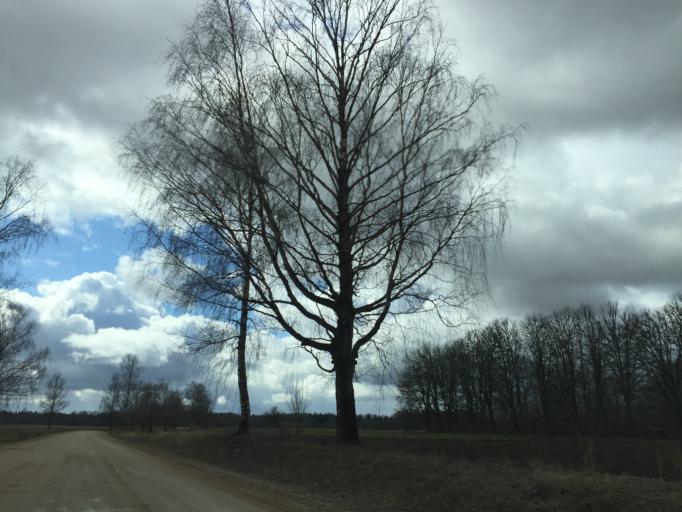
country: LV
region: Akniste
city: Akniste
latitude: 56.1151
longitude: 25.8869
